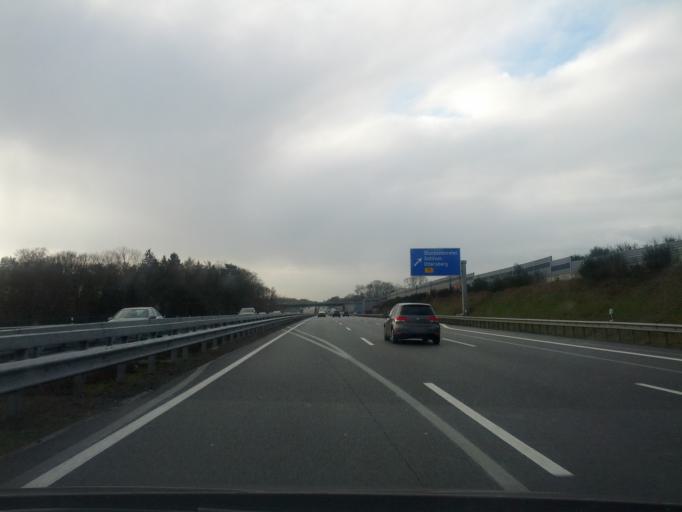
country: DE
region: Lower Saxony
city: Reessum
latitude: 53.1129
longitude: 9.2039
